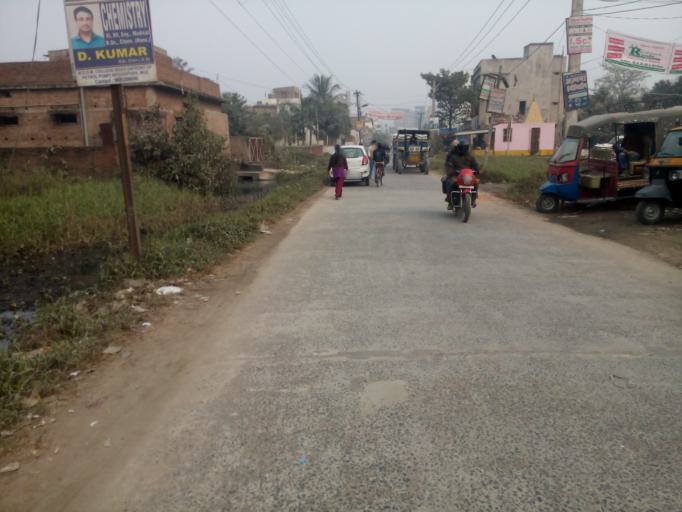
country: IN
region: Bihar
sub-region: Muzaffarpur
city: Muzaffarpur
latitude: 26.1028
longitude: 85.4038
